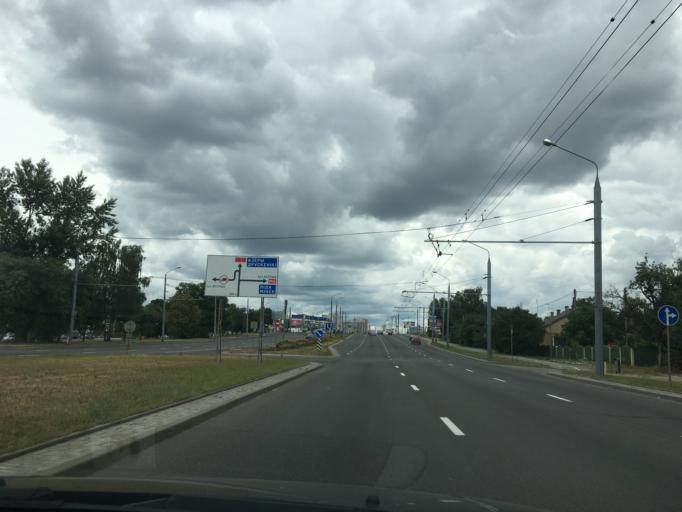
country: BY
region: Grodnenskaya
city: Hrodna
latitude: 53.6681
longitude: 23.8611
